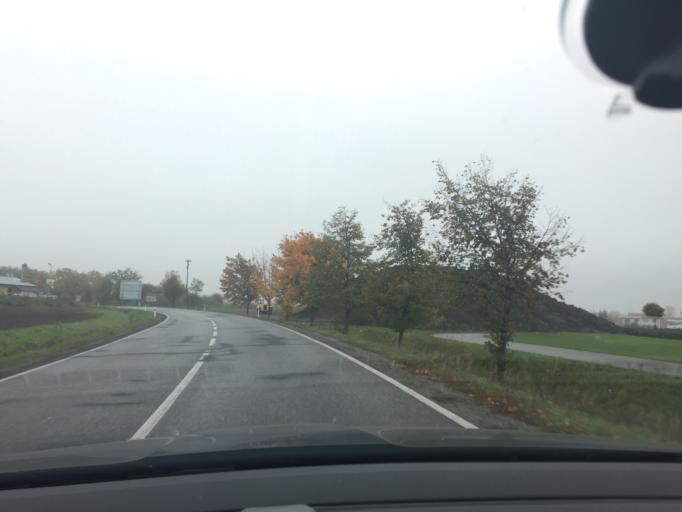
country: CZ
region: South Moravian
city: Rousinov
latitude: 49.1981
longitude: 16.8793
